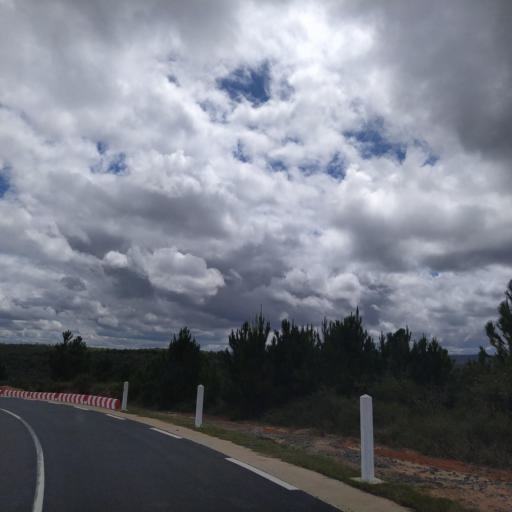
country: MG
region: Analamanga
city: Anjozorobe
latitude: -18.4808
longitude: 48.2655
